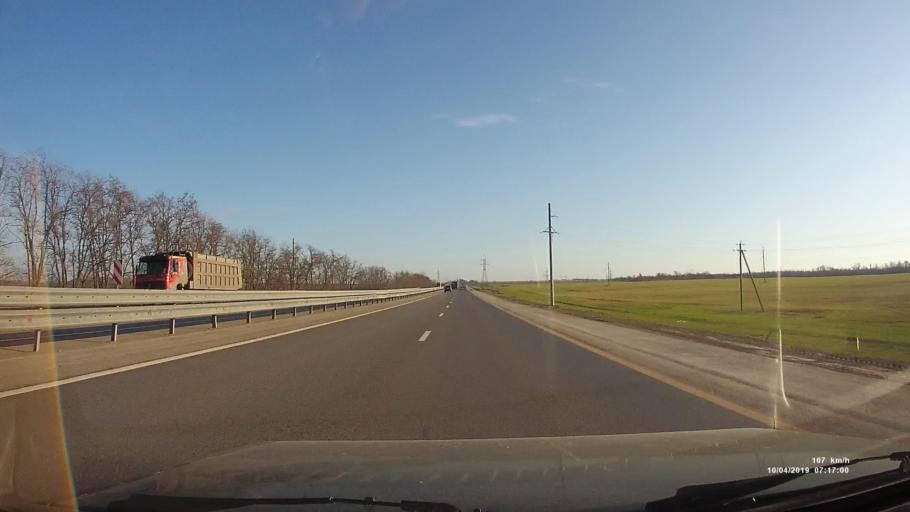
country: RU
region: Rostov
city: Ayutinskiy
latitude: 47.7783
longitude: 40.1607
